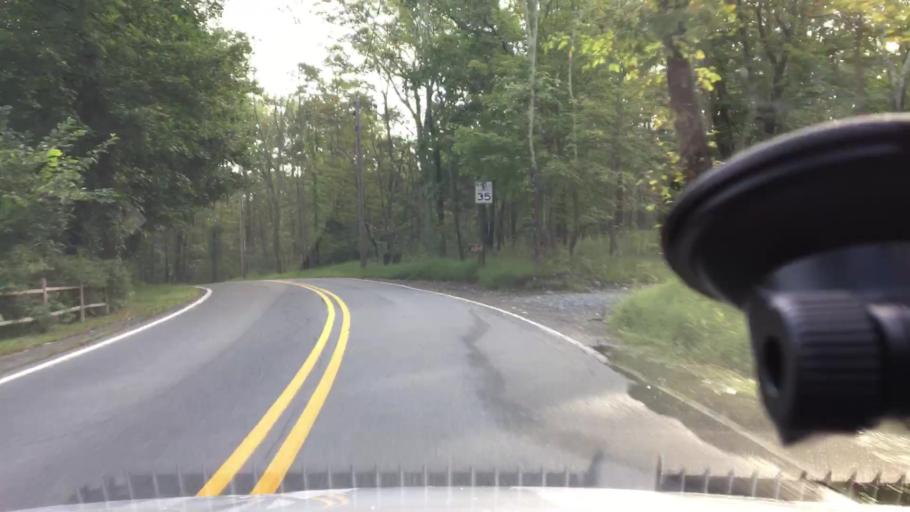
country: US
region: Pennsylvania
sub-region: Monroe County
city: Parkside
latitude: 41.1278
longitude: -75.2764
